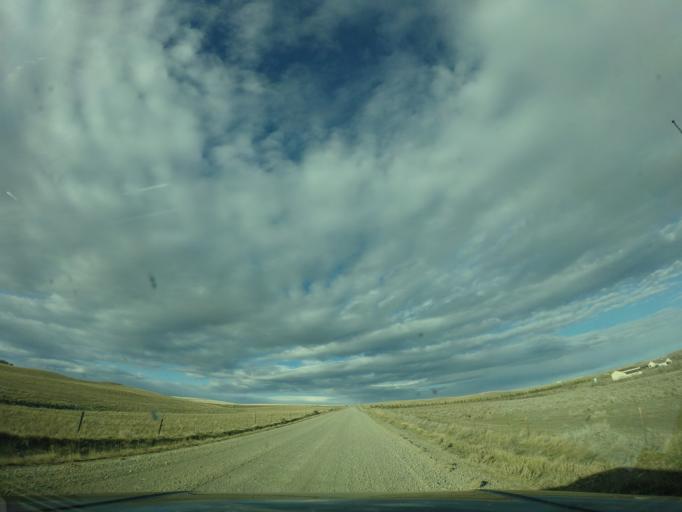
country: US
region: Montana
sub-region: Yellowstone County
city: Laurel
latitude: 45.8834
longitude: -108.8811
